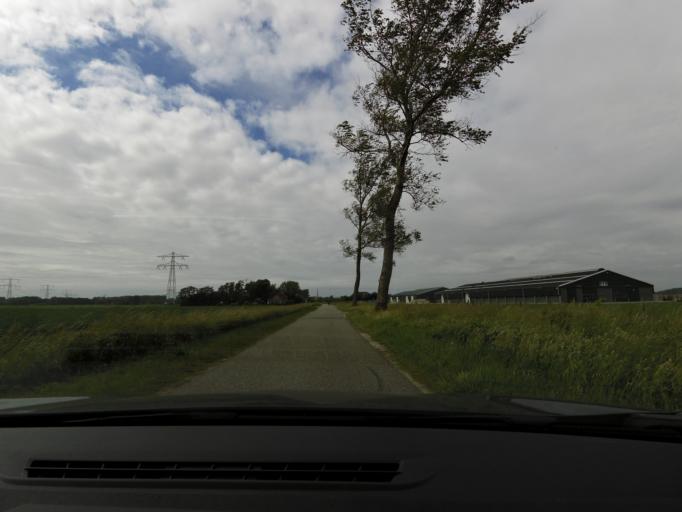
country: NL
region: South Holland
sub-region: Gemeente Brielle
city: Brielle
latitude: 51.9122
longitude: 4.1311
